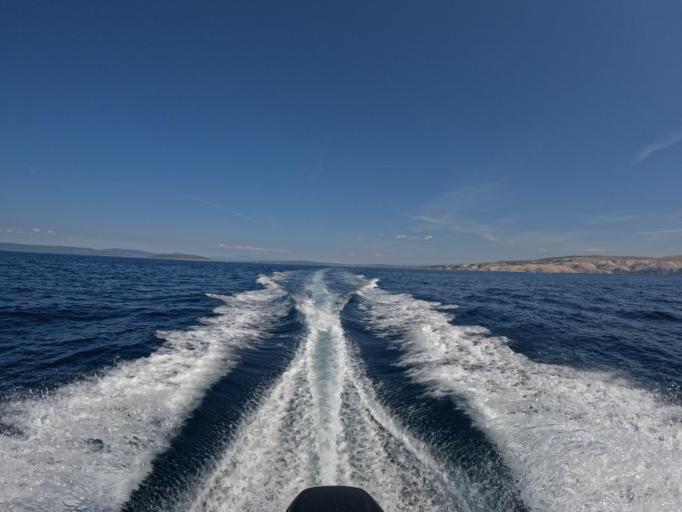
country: HR
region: Primorsko-Goranska
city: Punat
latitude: 44.9113
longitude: 14.6277
